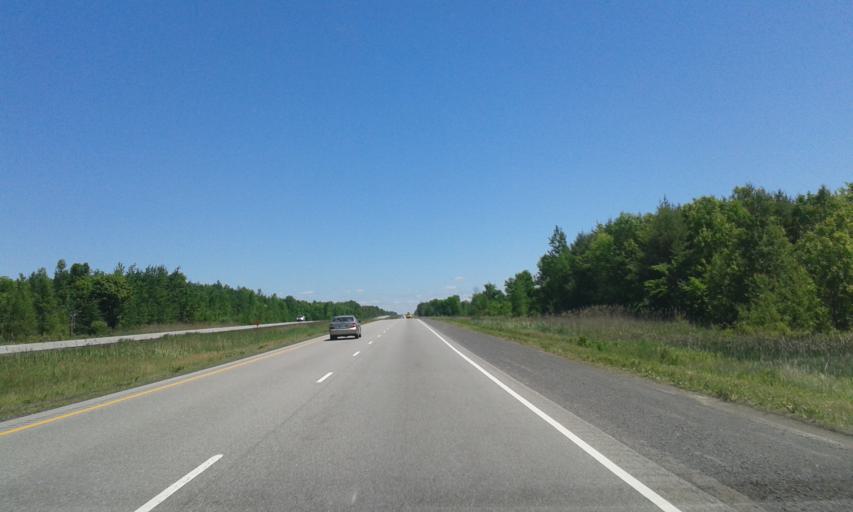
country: US
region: New York
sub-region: St. Lawrence County
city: Ogdensburg
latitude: 44.8264
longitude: -75.3799
